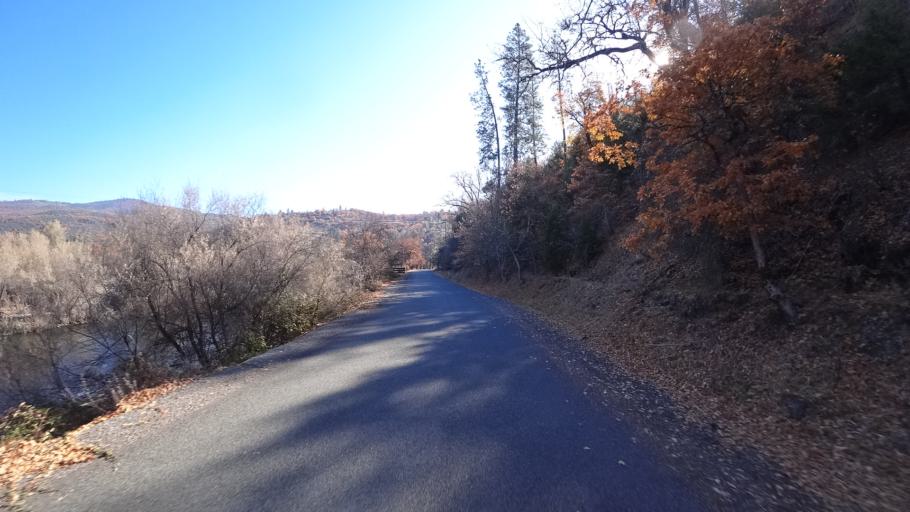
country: US
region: California
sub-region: Siskiyou County
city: Yreka
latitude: 41.8320
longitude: -122.8505
